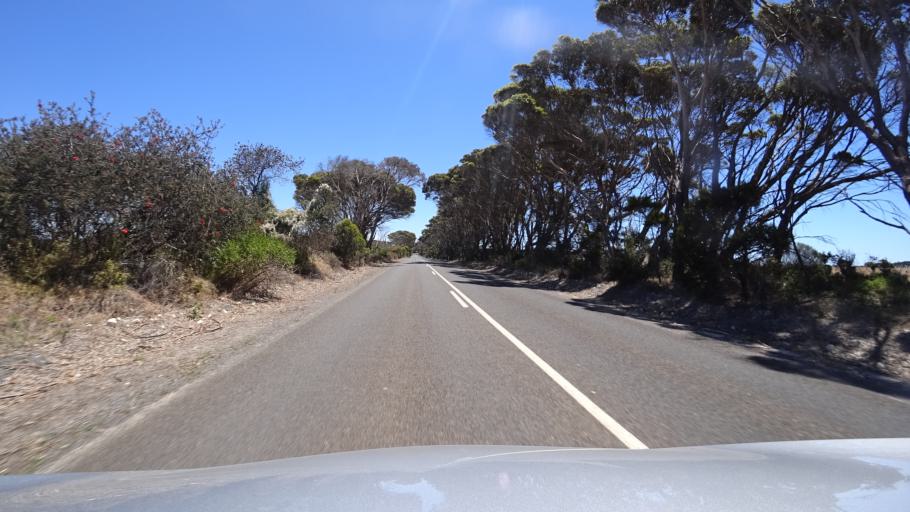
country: AU
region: South Australia
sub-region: Kangaroo Island
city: Kingscote
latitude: -35.7405
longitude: 137.9539
